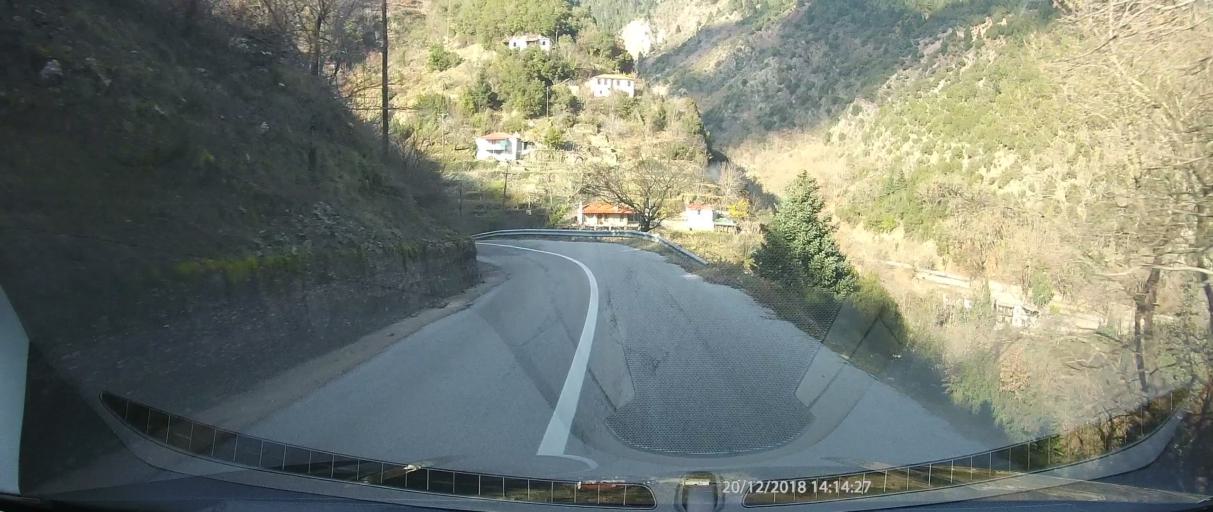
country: GR
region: West Greece
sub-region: Nomos Aitolias kai Akarnanias
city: Thermo
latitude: 38.7479
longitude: 21.6527
